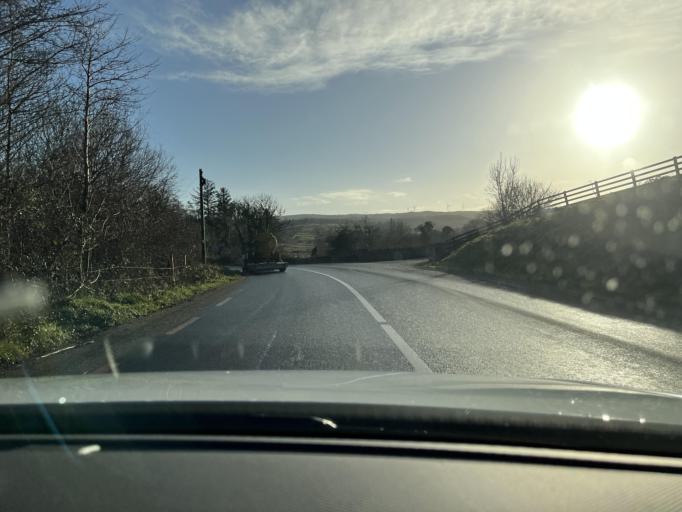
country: IE
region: Connaught
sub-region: County Leitrim
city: Manorhamilton
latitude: 54.2090
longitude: -8.2055
